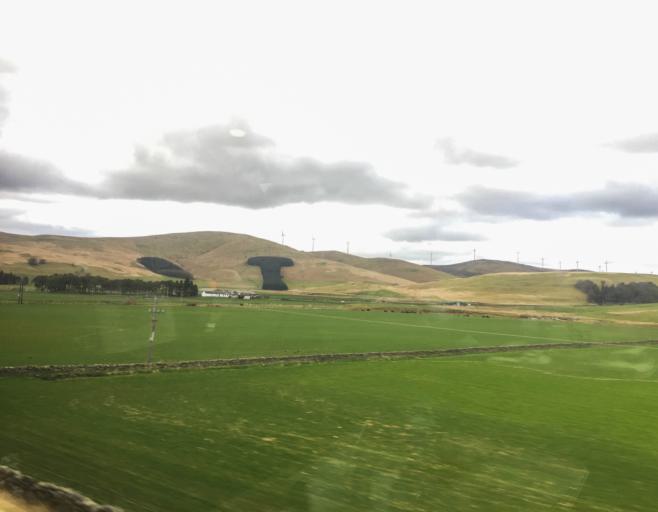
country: GB
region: Scotland
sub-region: South Lanarkshire
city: Biggar
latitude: 55.4693
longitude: -3.6504
